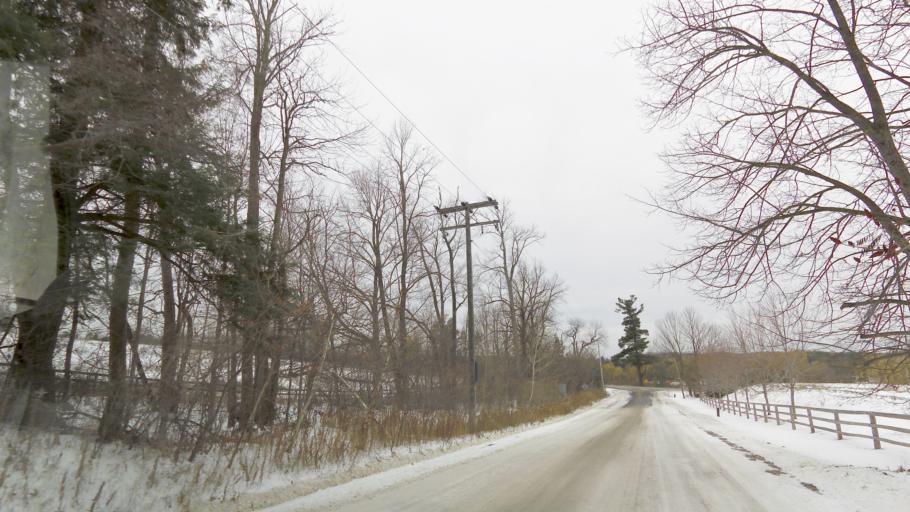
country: CA
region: Ontario
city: Bradford West Gwillimbury
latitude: 43.9443
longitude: -79.6355
